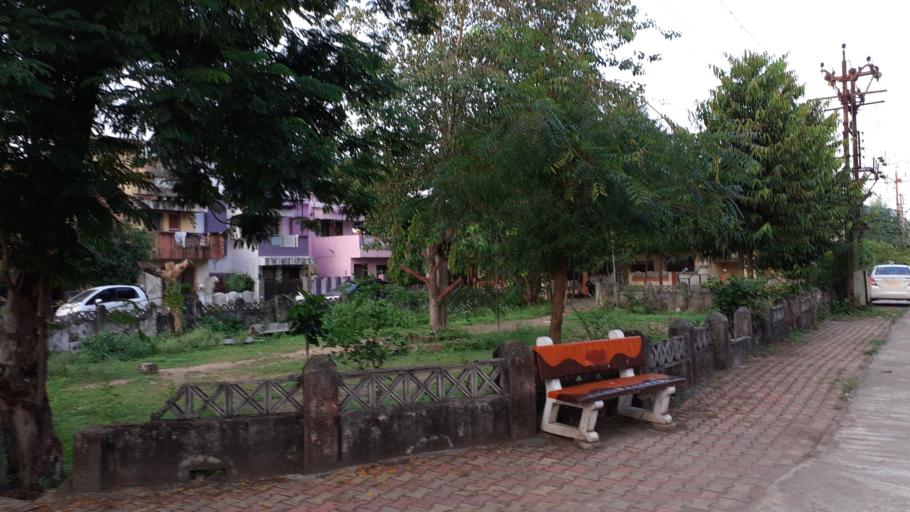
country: IN
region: Maharashtra
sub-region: Chandrapur
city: Chandrapur
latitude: 19.9686
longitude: 79.2741
